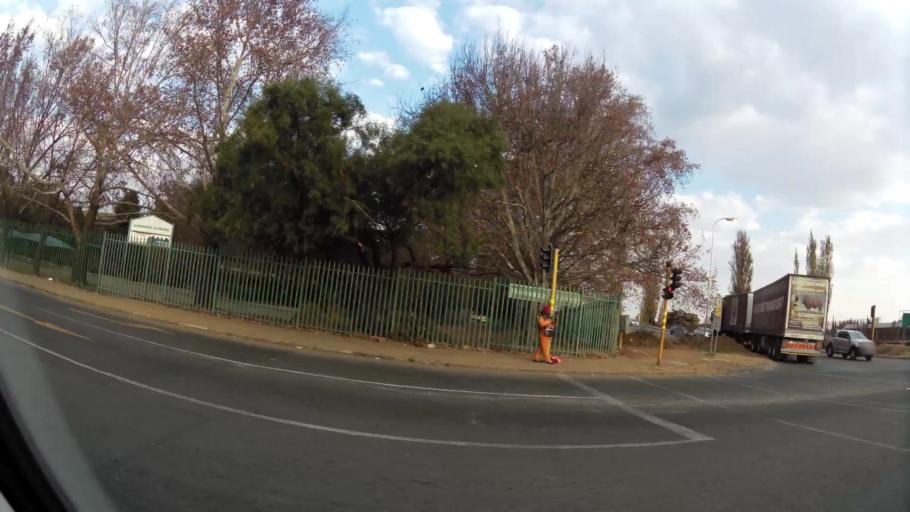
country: ZA
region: Gauteng
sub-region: Ekurhuleni Metropolitan Municipality
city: Germiston
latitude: -26.2512
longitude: 28.2001
